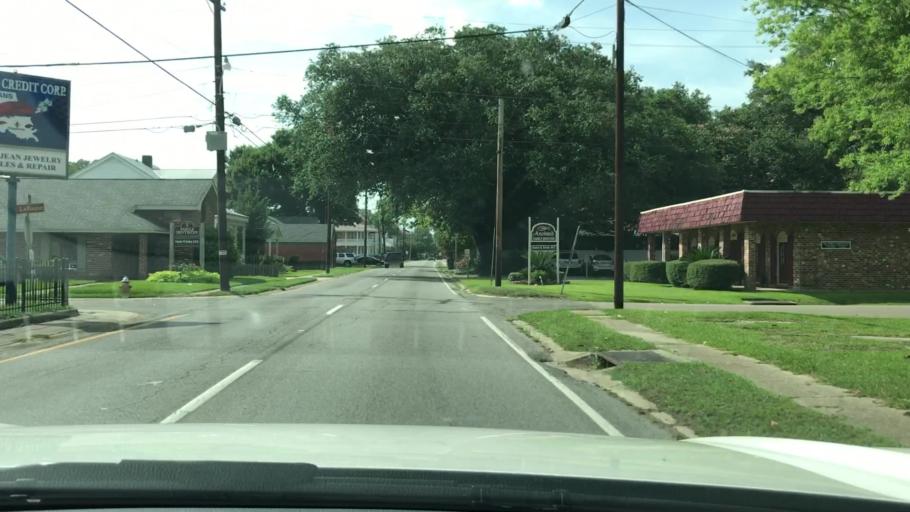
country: US
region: Louisiana
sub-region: Iberville Parish
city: Plaquemine
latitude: 30.2870
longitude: -91.2313
